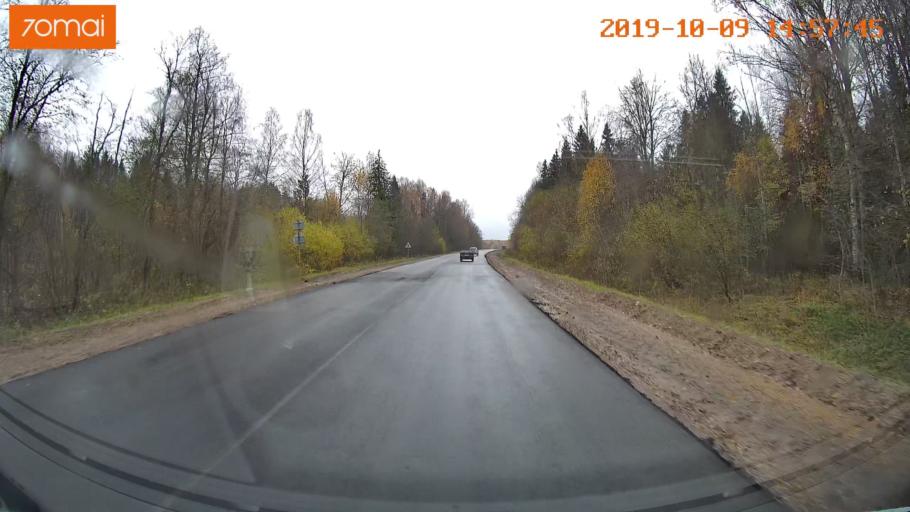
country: RU
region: Kostroma
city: Chistyye Bory
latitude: 58.3344
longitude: 41.6524
